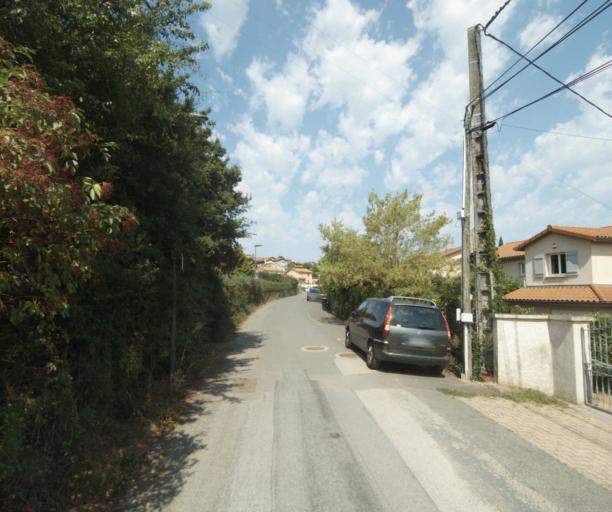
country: FR
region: Rhone-Alpes
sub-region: Departement du Rhone
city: Lentilly
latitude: 45.8379
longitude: 4.6558
